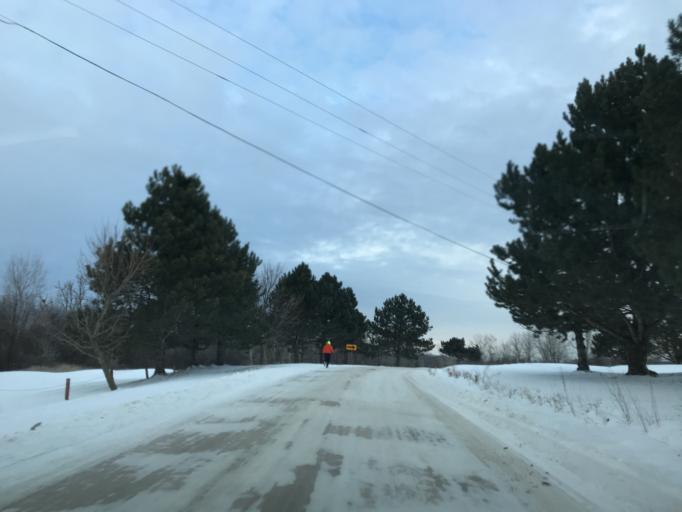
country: US
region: Michigan
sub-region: Livingston County
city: Whitmore Lake
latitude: 42.4007
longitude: -83.7450
